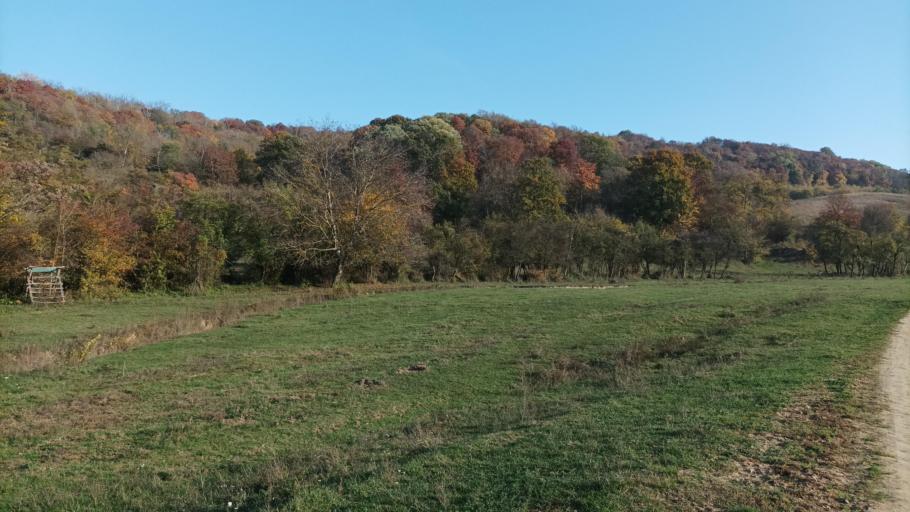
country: HU
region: Tolna
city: Szentgalpuszta
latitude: 46.3352
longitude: 18.6068
